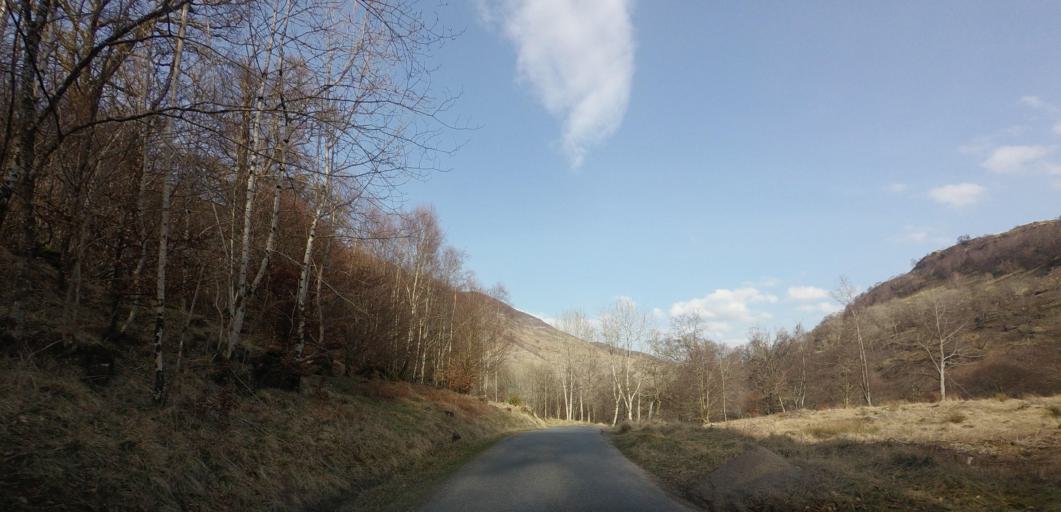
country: GB
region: Scotland
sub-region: Perth and Kinross
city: Aberfeldy
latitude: 56.5999
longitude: -4.1016
